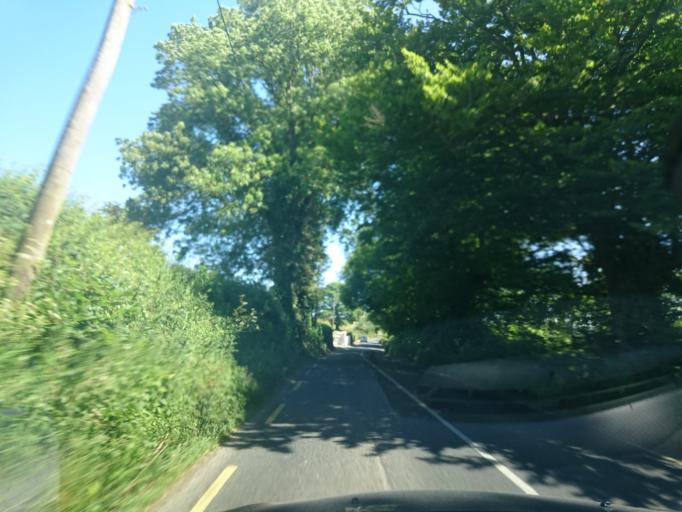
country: IE
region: Leinster
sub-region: County Carlow
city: Bagenalstown
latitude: 52.6278
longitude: -7.0212
